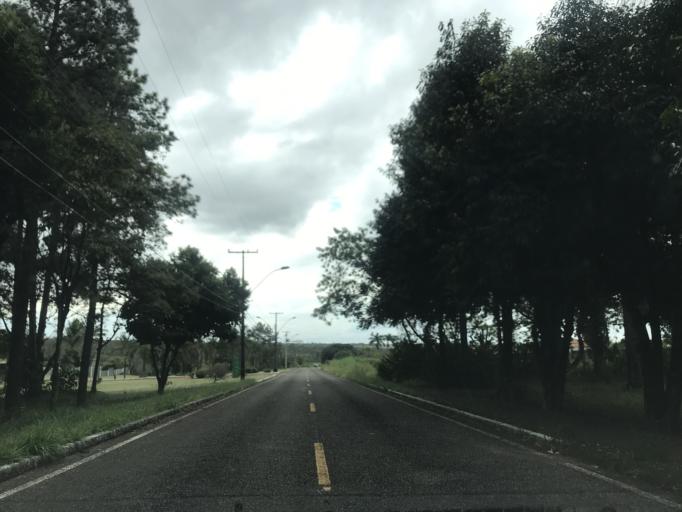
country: BR
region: Federal District
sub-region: Brasilia
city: Brasilia
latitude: -15.8942
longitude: -47.9314
